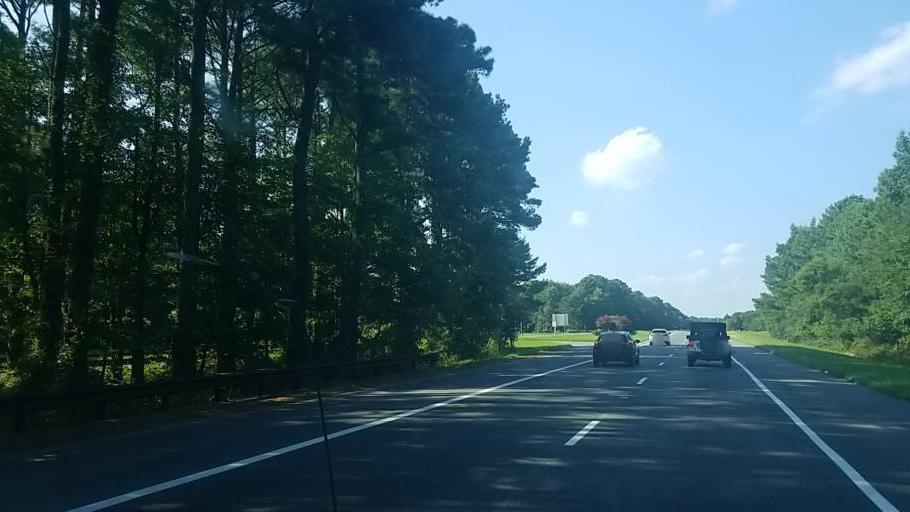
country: US
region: Maryland
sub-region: Worcester County
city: Berlin
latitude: 38.3535
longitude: -75.2141
